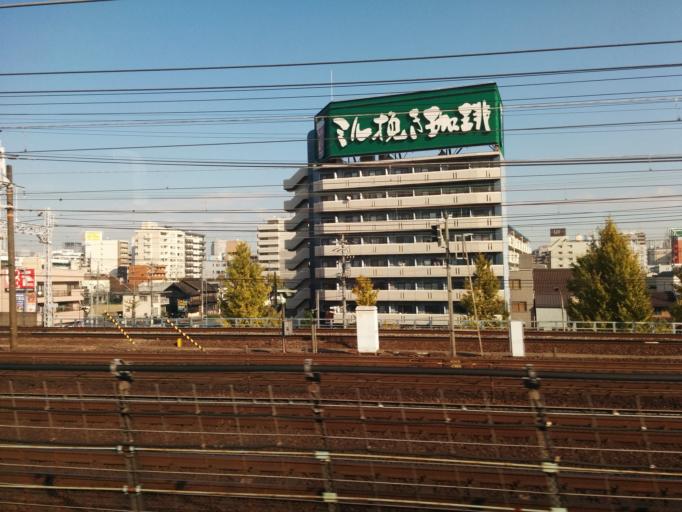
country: JP
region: Aichi
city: Nagoya-shi
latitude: 35.1586
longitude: 136.8866
